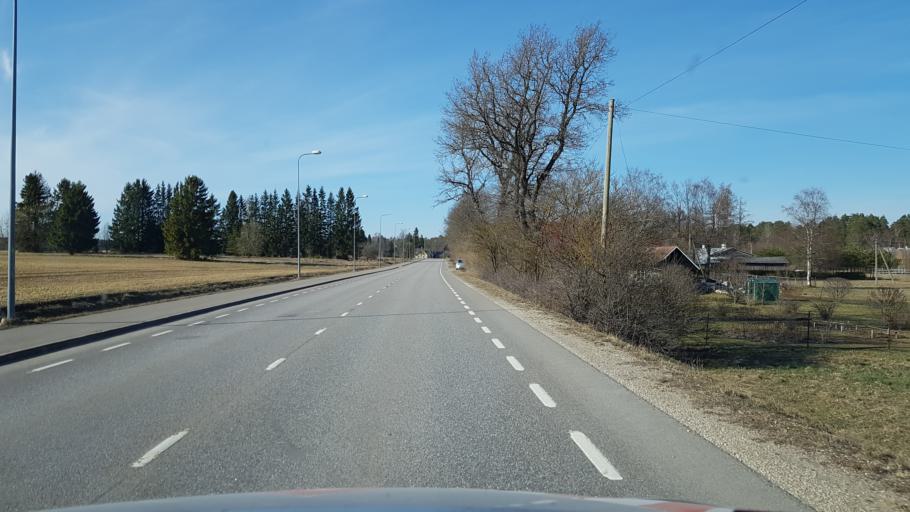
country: EE
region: Laeaene-Virumaa
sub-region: Vinni vald
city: Vinni
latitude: 59.1593
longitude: 26.5875
